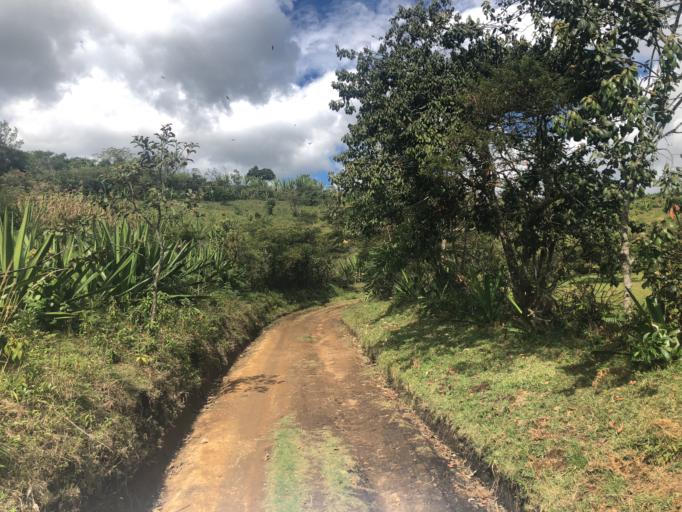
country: CO
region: Cauca
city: Silvia
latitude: 2.6871
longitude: -76.4396
